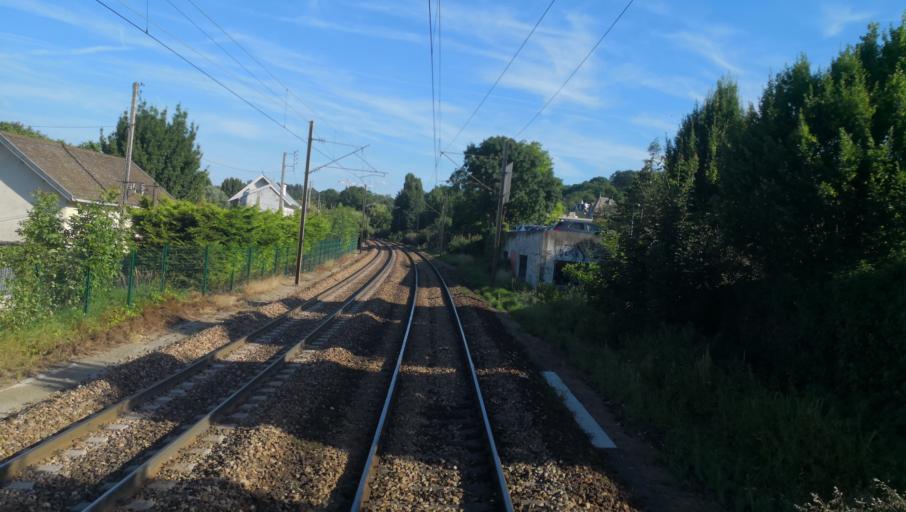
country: FR
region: Ile-de-France
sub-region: Departement des Yvelines
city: Villennes-sur-Seine
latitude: 48.9374
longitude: 1.9999
